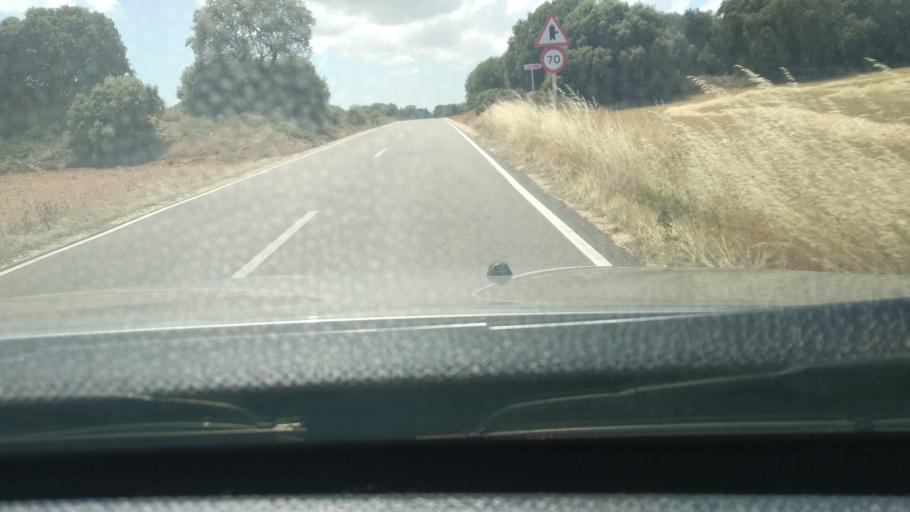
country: ES
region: Castille and Leon
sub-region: Provincia de Burgos
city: Avellanosa de Muno
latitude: 41.9704
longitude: -3.8116
